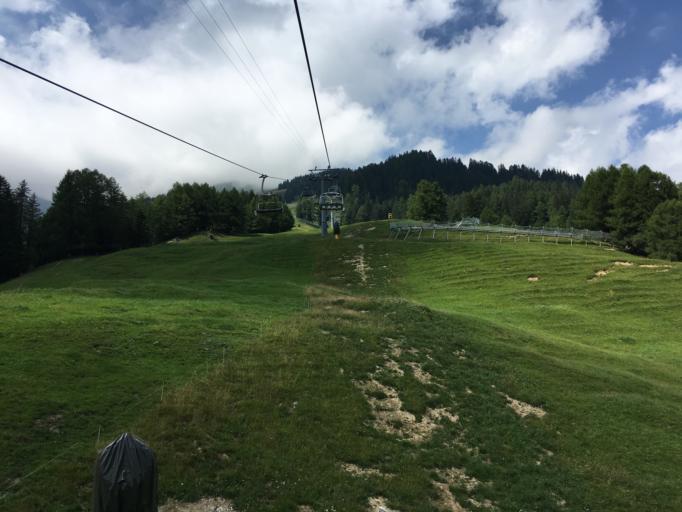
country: CH
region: Grisons
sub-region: Plessur District
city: Churwalden
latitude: 46.7811
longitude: 9.5298
